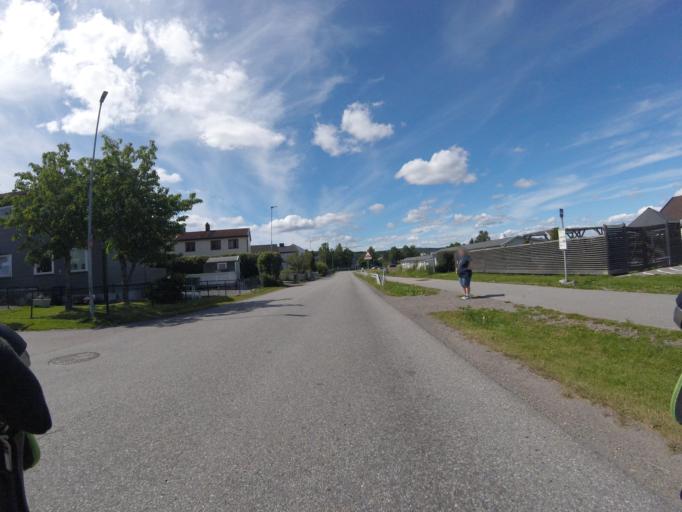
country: NO
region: Akershus
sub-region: Skedsmo
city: Lillestrom
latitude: 59.9505
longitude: 11.0195
